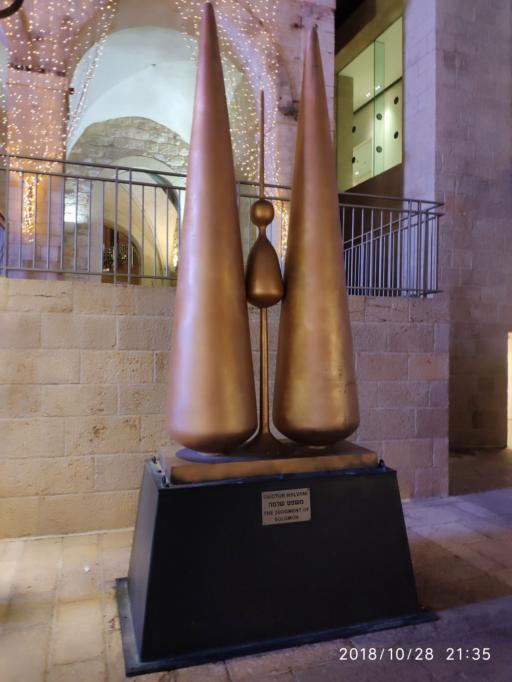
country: IL
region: Jerusalem
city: West Jerusalem
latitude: 31.7779
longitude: 35.2233
